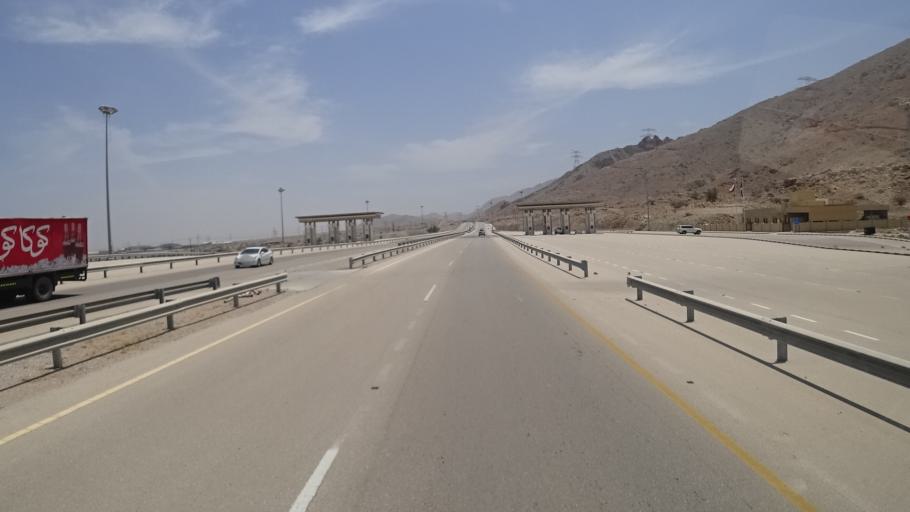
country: OM
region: Ash Sharqiyah
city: Sur
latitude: 22.6690
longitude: 59.3891
